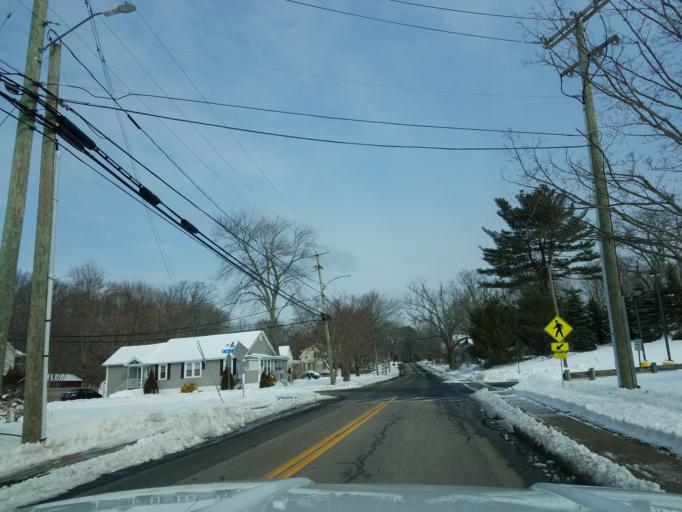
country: US
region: Connecticut
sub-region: Middlesex County
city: East Hampton
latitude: 41.5841
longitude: -72.5068
